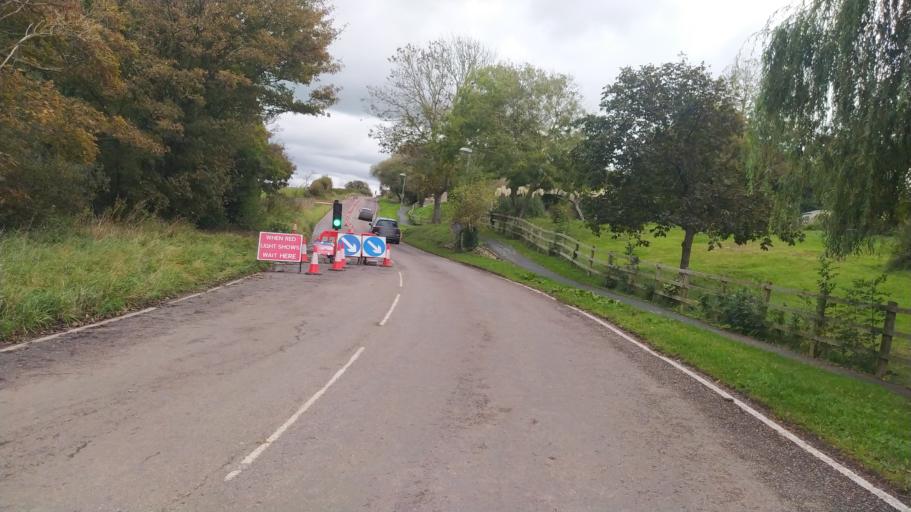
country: GB
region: England
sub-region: Dorset
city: Lyme Regis
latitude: 50.7380
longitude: -2.8933
